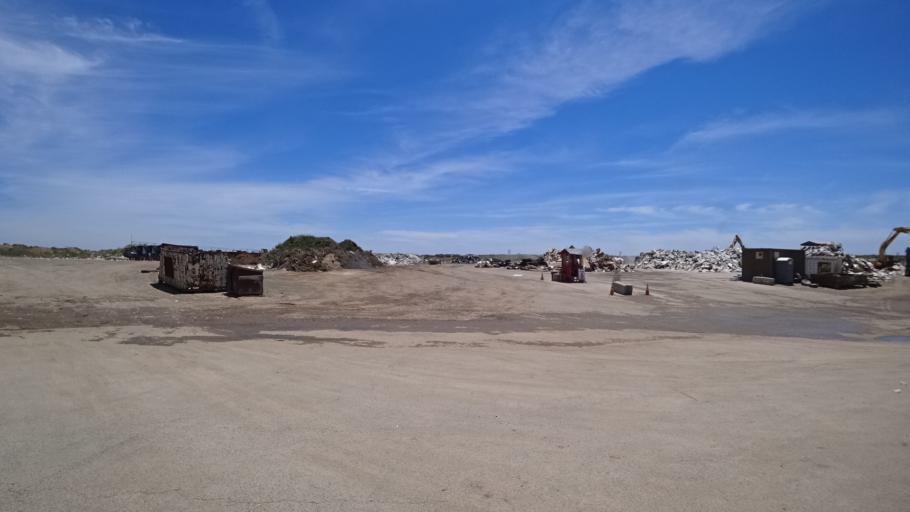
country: US
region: California
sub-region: Sacramento County
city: Rosemont
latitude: 38.5273
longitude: -121.3817
